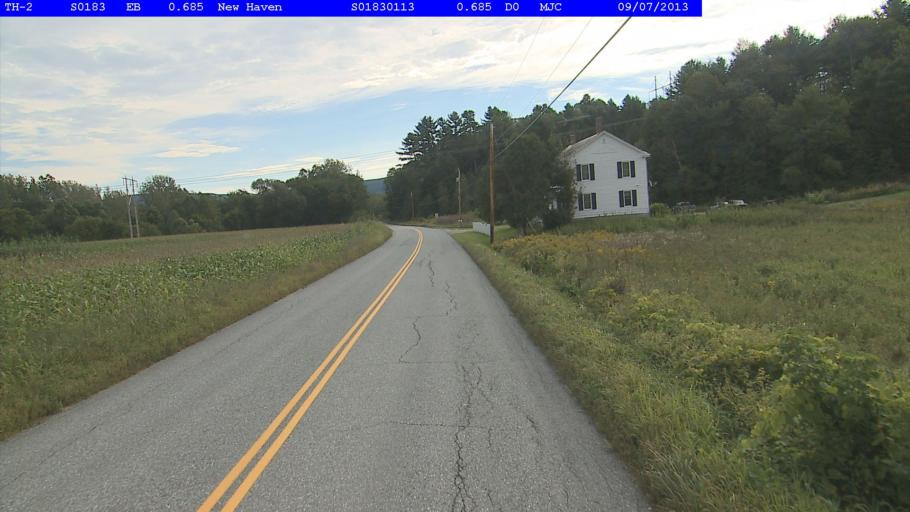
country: US
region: Vermont
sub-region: Addison County
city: Middlebury (village)
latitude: 44.0587
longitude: -73.1548
